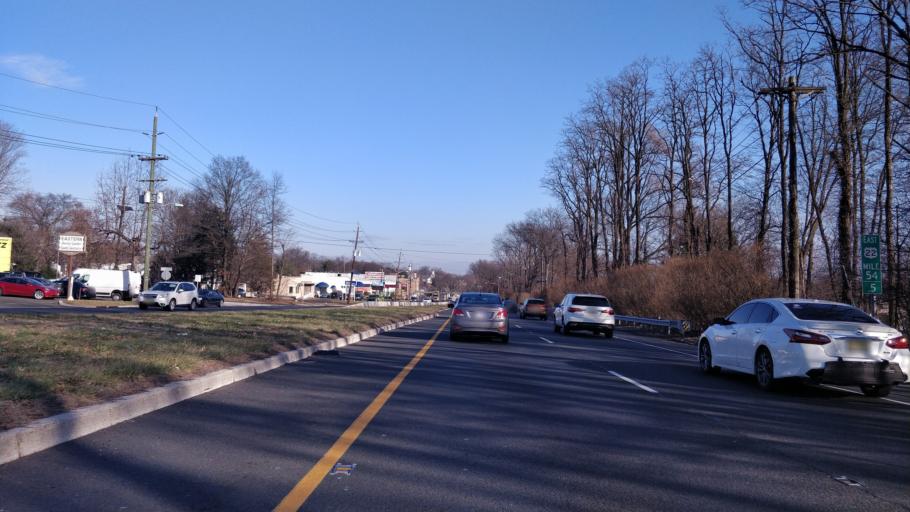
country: US
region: New Jersey
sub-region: Union County
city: Kenilworth
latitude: 40.6916
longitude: -74.2828
